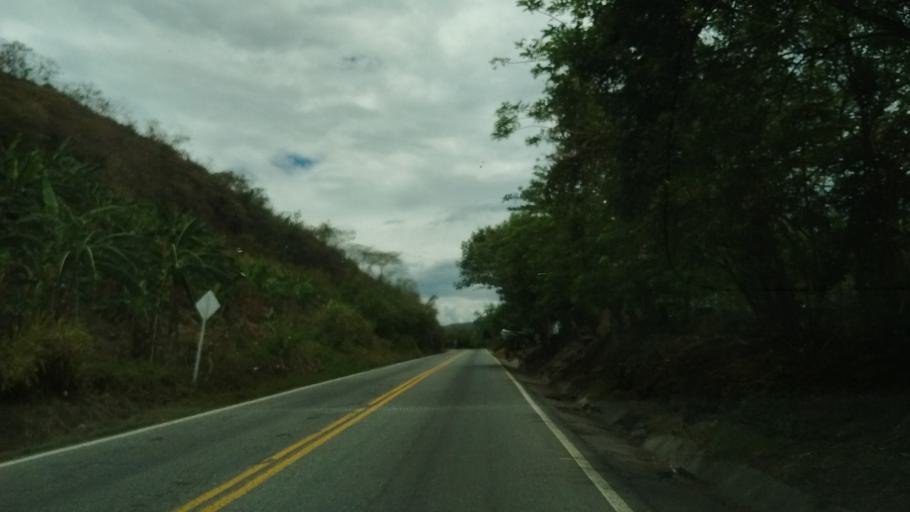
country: CO
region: Cauca
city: La Sierra
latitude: 2.2119
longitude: -76.7989
